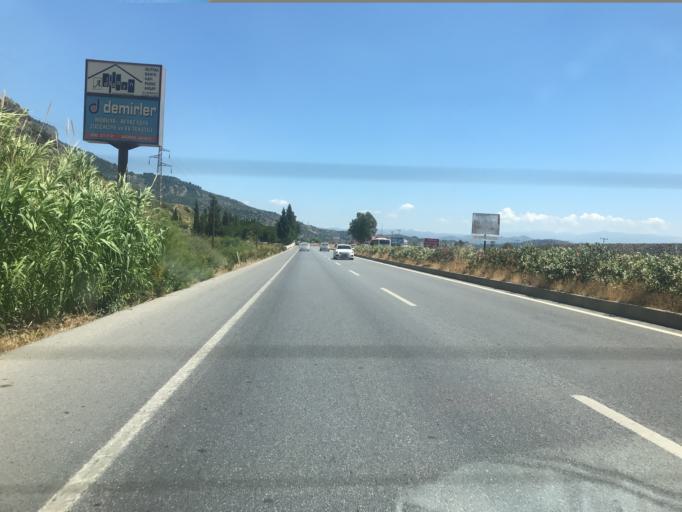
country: TR
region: Aydin
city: Ortaklar
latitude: 37.8105
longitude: 27.4817
